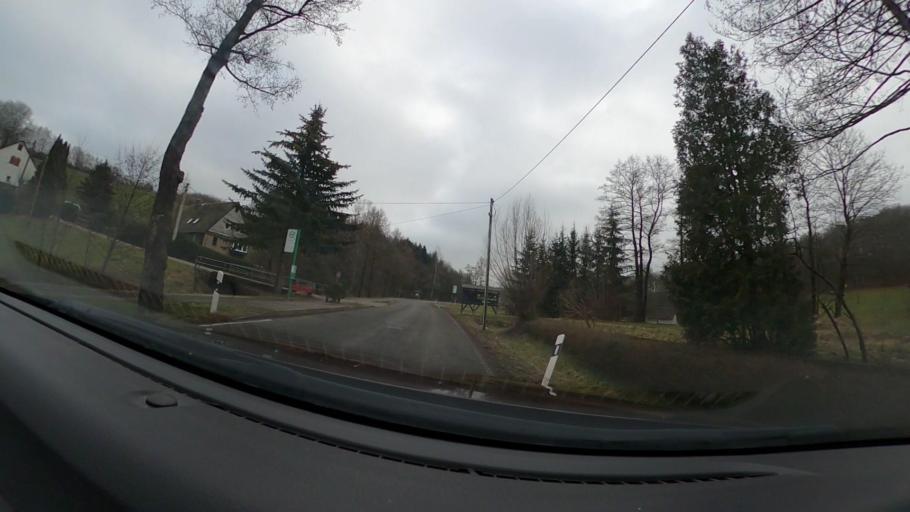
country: DE
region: Saxony
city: Oberschona
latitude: 50.8892
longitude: 13.2723
